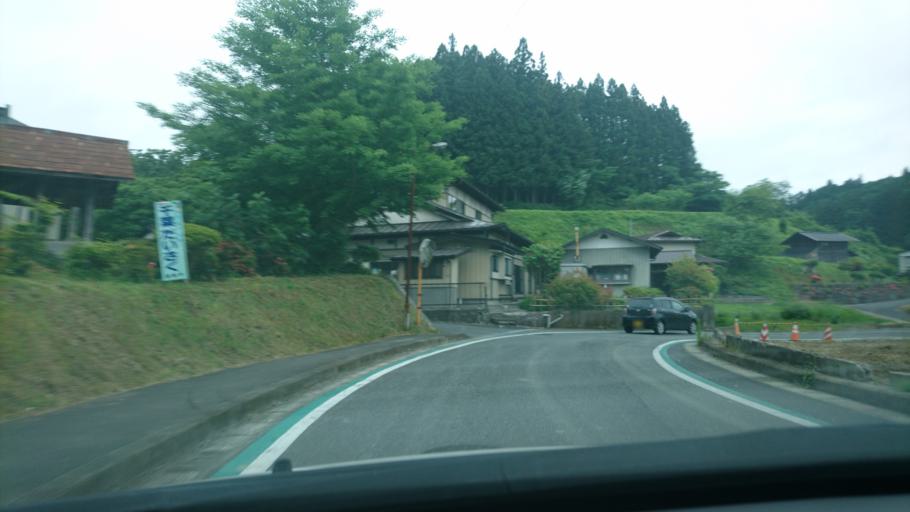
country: JP
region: Iwate
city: Ichinoseki
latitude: 38.9129
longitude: 141.1060
